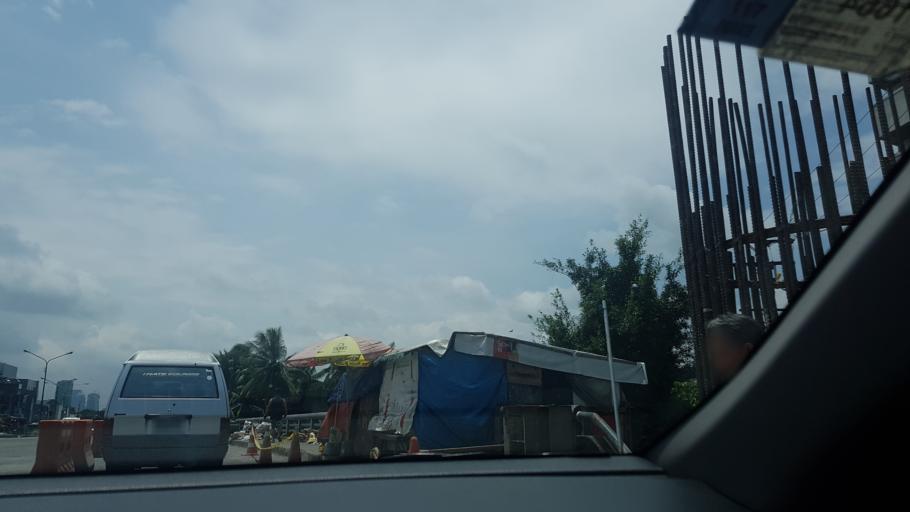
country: PH
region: Metro Manila
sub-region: San Juan
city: San Juan
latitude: 14.6046
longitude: 121.0197
